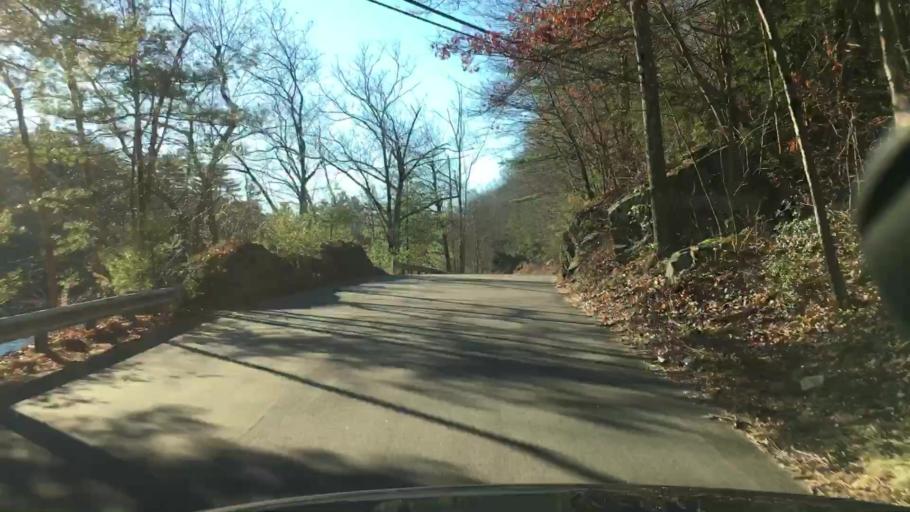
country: US
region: Connecticut
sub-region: Tolland County
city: Stafford Springs
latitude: 41.9700
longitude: -72.2979
